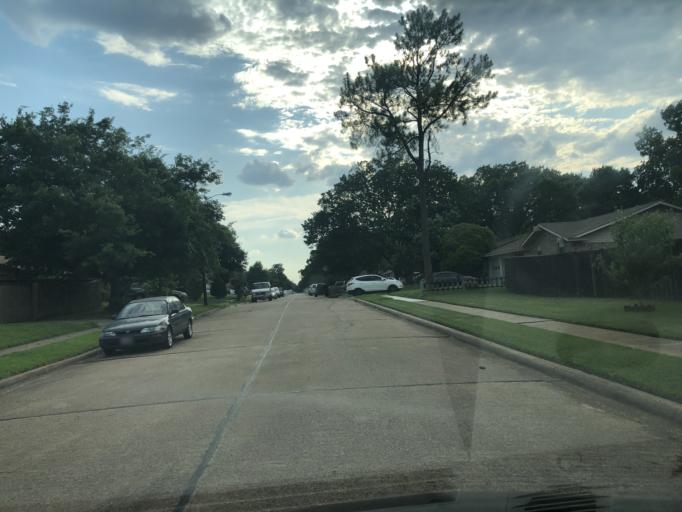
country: US
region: Texas
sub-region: Dallas County
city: Irving
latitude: 32.7891
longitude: -96.9695
